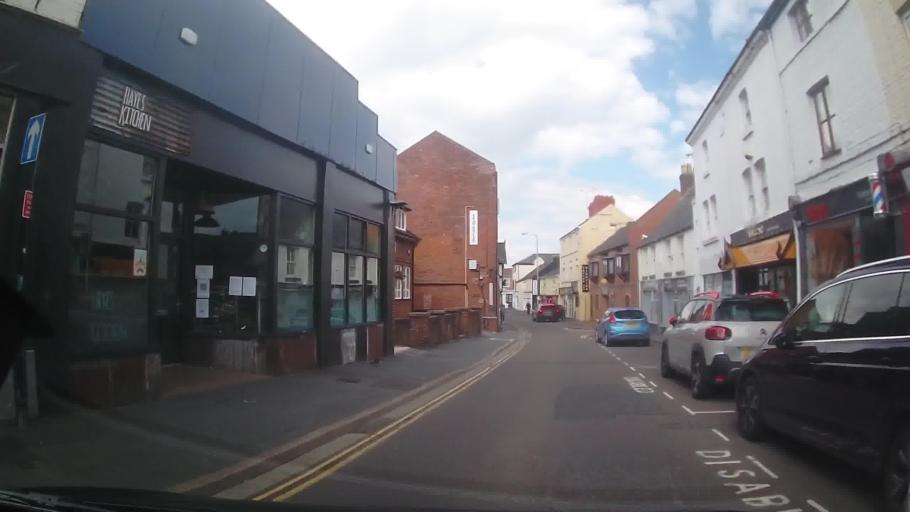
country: GB
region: England
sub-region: Shropshire
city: Oswestry
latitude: 52.8606
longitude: -3.0536
